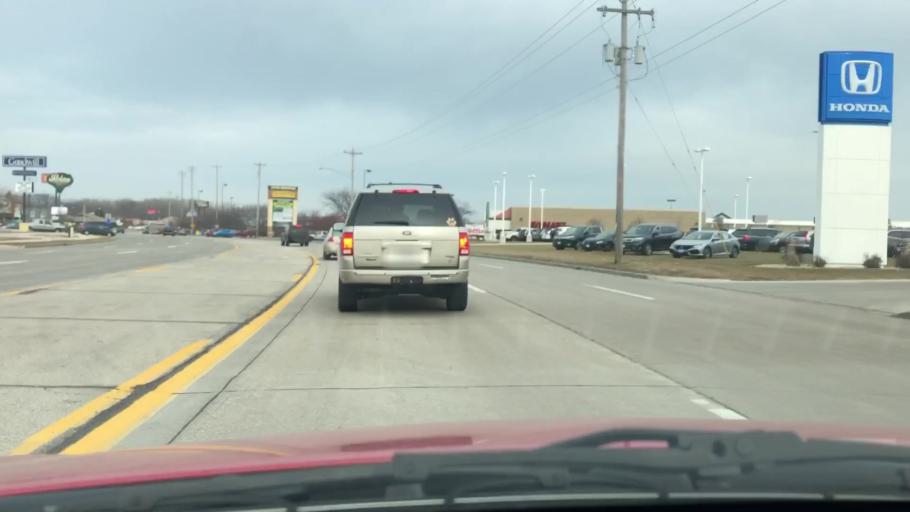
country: US
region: Wisconsin
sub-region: Brown County
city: Ashwaubenon
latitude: 44.4720
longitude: -88.0752
